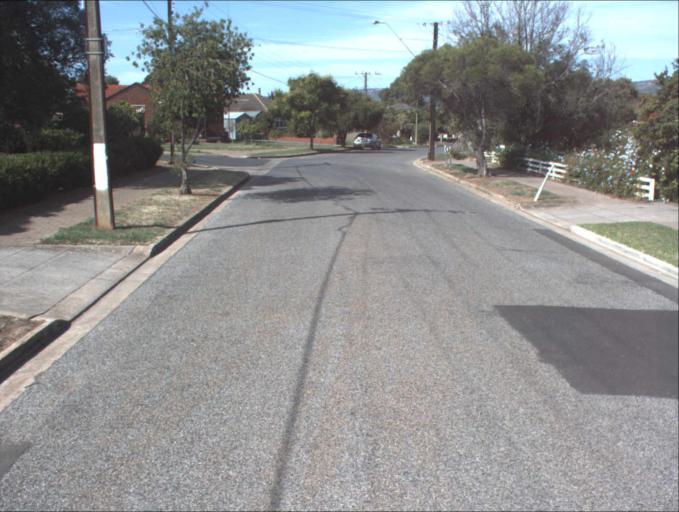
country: AU
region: South Australia
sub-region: Port Adelaide Enfield
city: Klemzig
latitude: -34.8707
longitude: 138.6474
